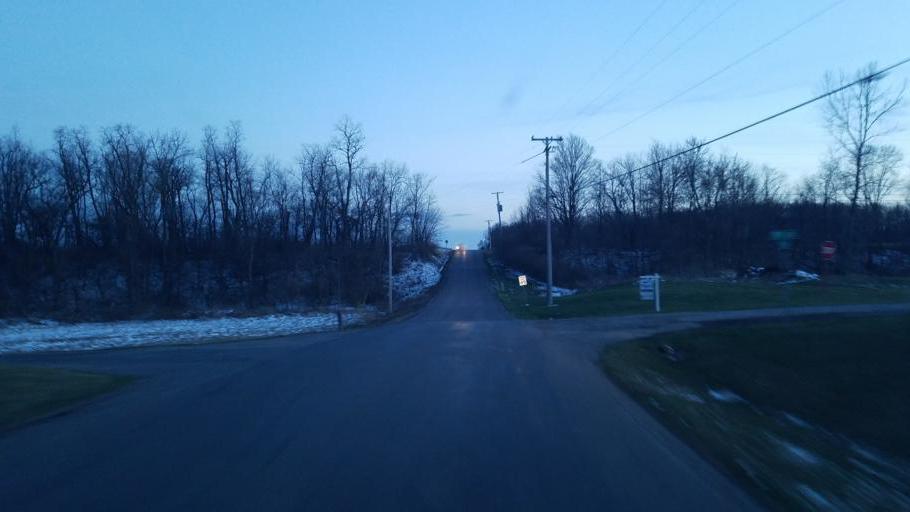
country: US
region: Ohio
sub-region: Ashland County
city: Ashland
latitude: 40.8411
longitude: -82.2795
